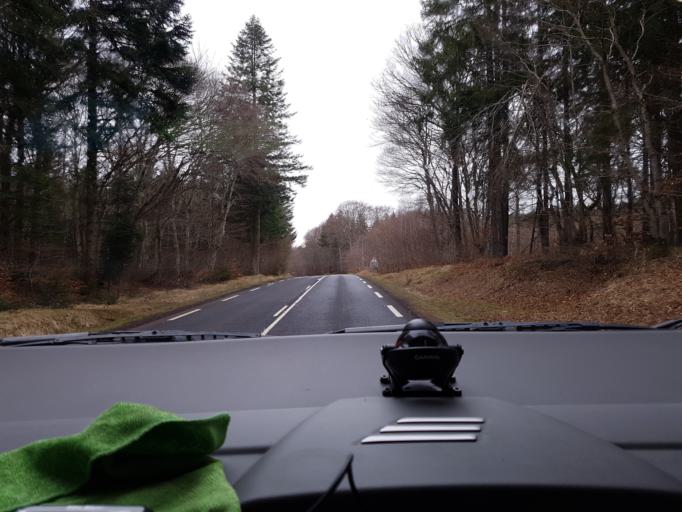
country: FR
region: Auvergne
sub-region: Departement du Puy-de-Dome
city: Charbonnieres-les-Varennes
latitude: 45.8605
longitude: 2.9549
